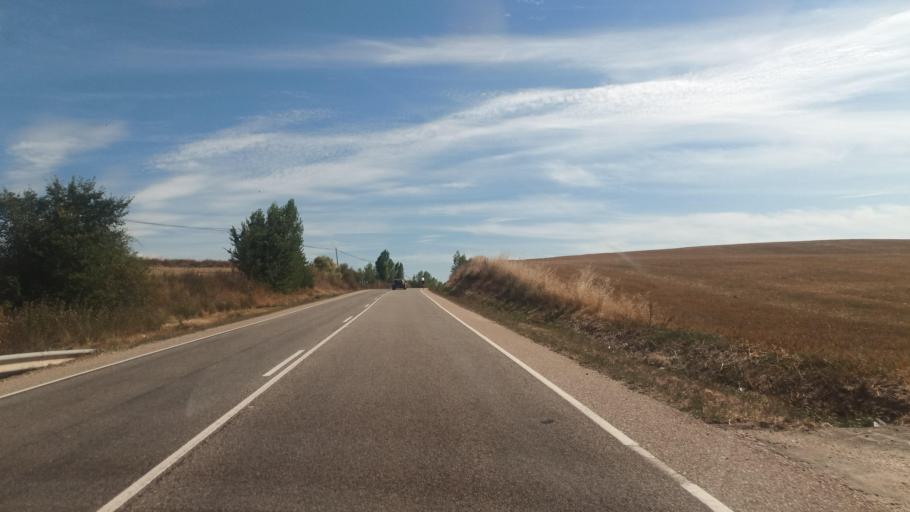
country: ES
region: Castille and Leon
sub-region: Provincia de Burgos
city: Aguilar de Bureba
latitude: 42.5739
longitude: -3.3320
